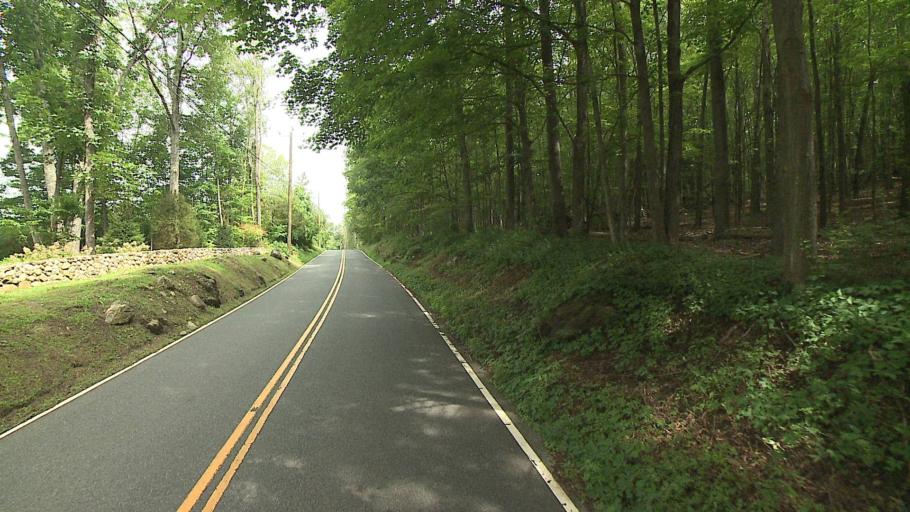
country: US
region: Connecticut
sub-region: Litchfield County
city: New Milford
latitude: 41.5870
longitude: -73.3219
